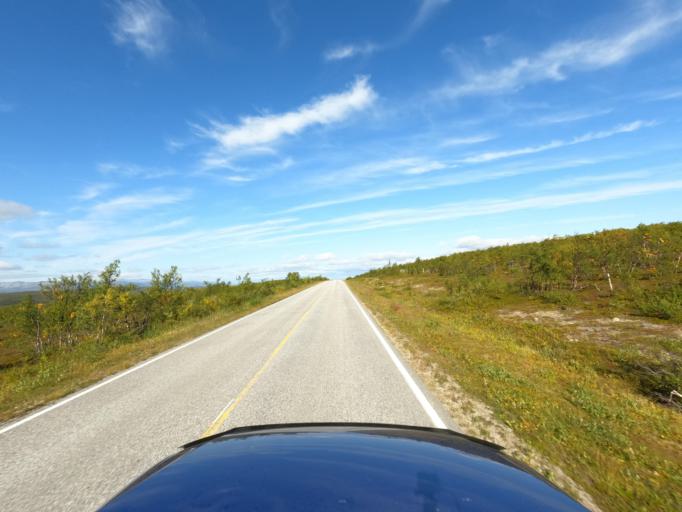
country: NO
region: Finnmark Fylke
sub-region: Karasjok
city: Karasjohka
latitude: 69.7142
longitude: 25.2403
